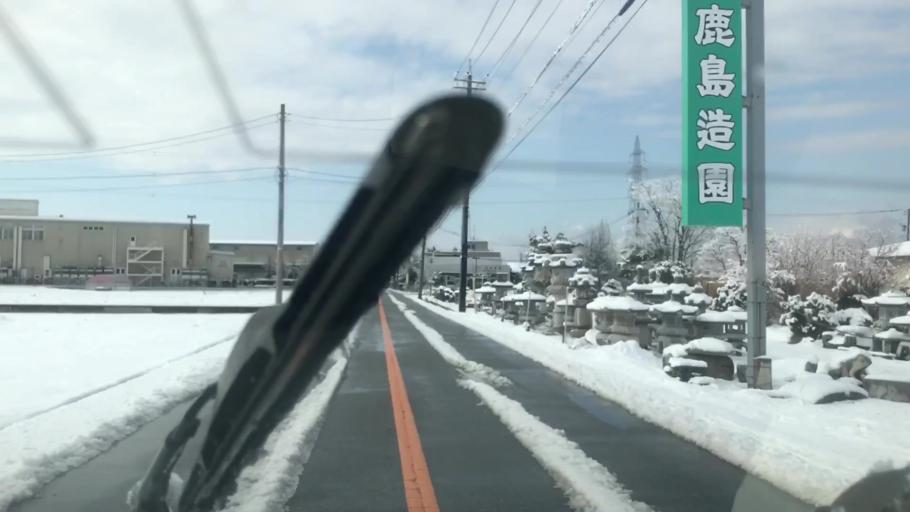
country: JP
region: Toyama
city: Toyama-shi
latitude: 36.6318
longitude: 137.2261
